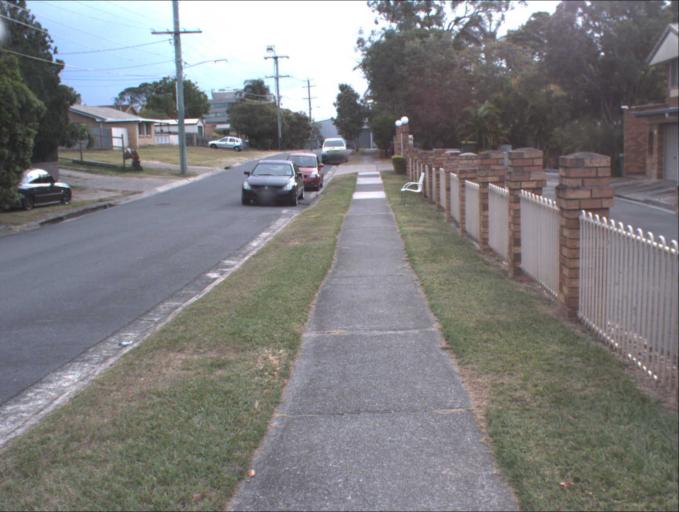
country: AU
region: Queensland
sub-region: Logan
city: Springwood
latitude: -27.6164
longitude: 153.1292
